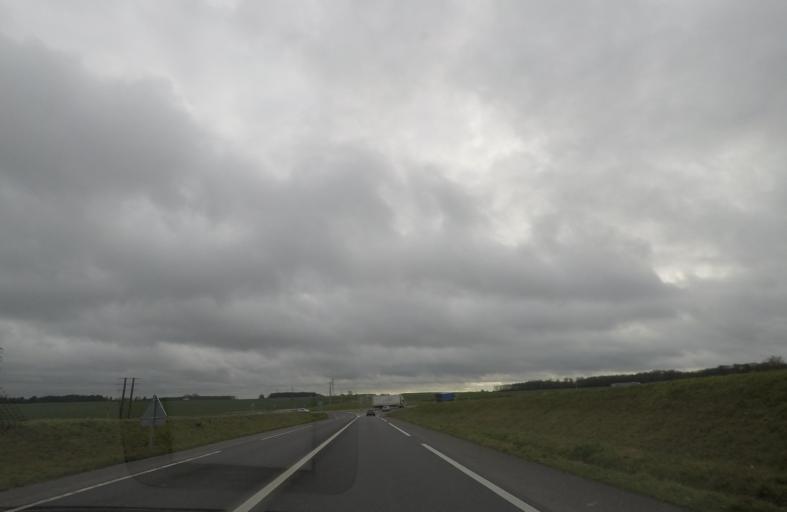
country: FR
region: Centre
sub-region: Departement du Loir-et-Cher
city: Vendome
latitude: 47.7729
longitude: 1.0580
